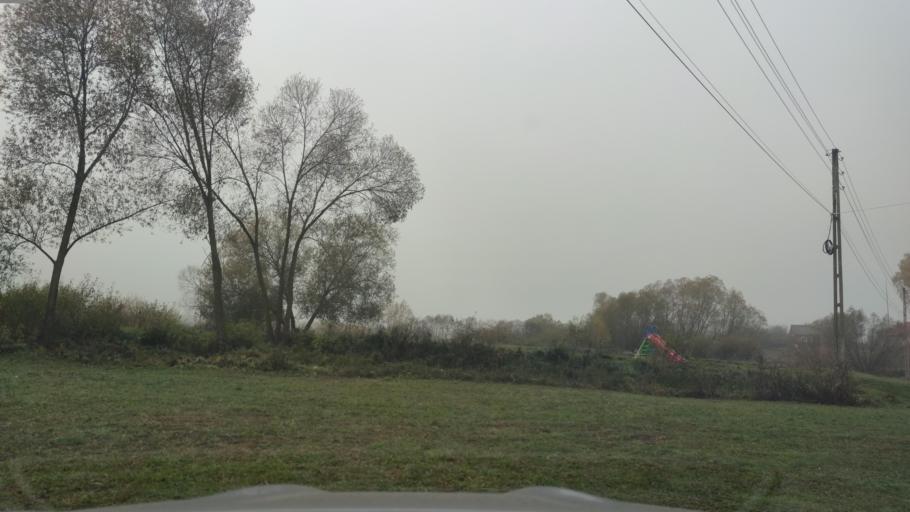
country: RO
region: Harghita
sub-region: Comuna Remetea
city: Remetea
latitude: 46.8133
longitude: 25.4219
